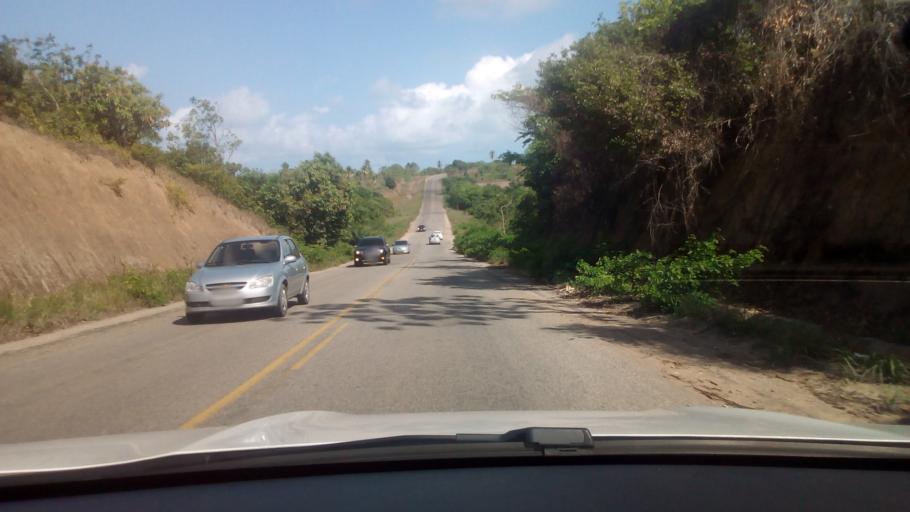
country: BR
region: Paraiba
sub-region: Conde
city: Conde
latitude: -7.2395
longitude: -34.8400
